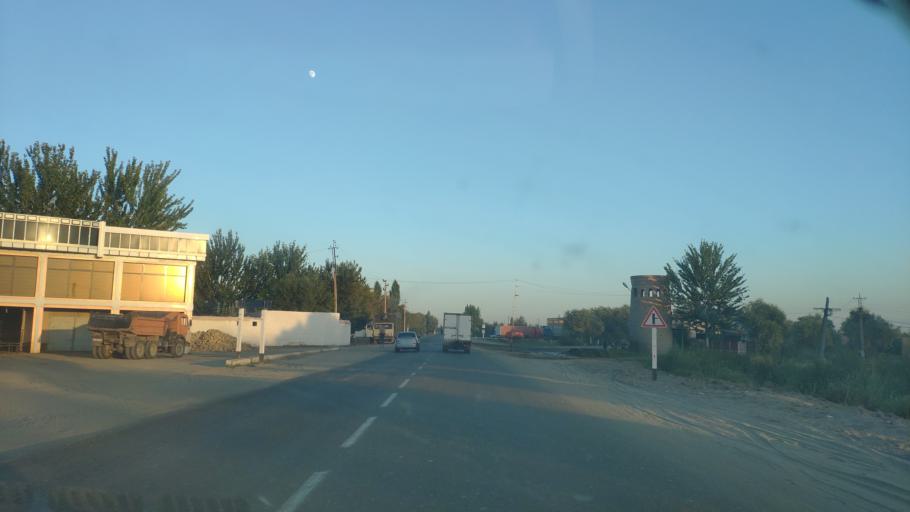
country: UZ
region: Karakalpakstan
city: To'rtko'l Shahri
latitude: 41.5676
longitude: 60.9516
